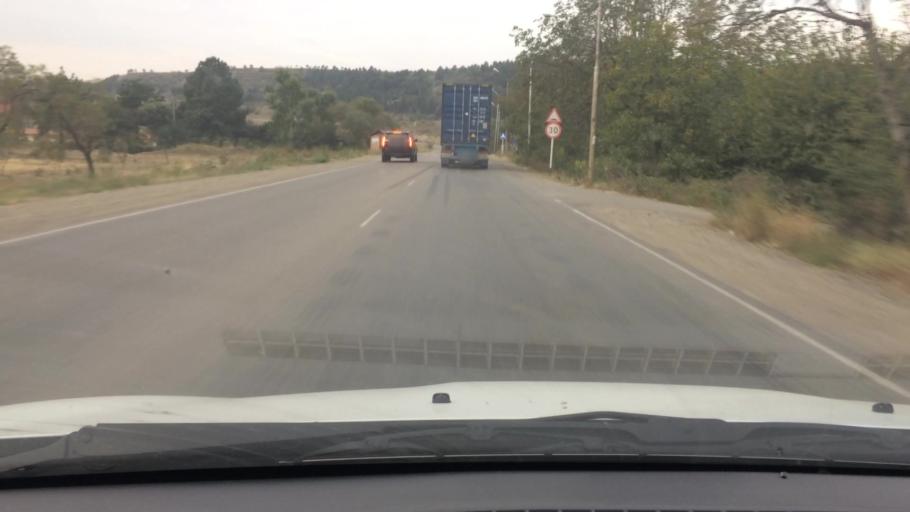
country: GE
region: T'bilisi
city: Tbilisi
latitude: 41.6055
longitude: 44.7818
